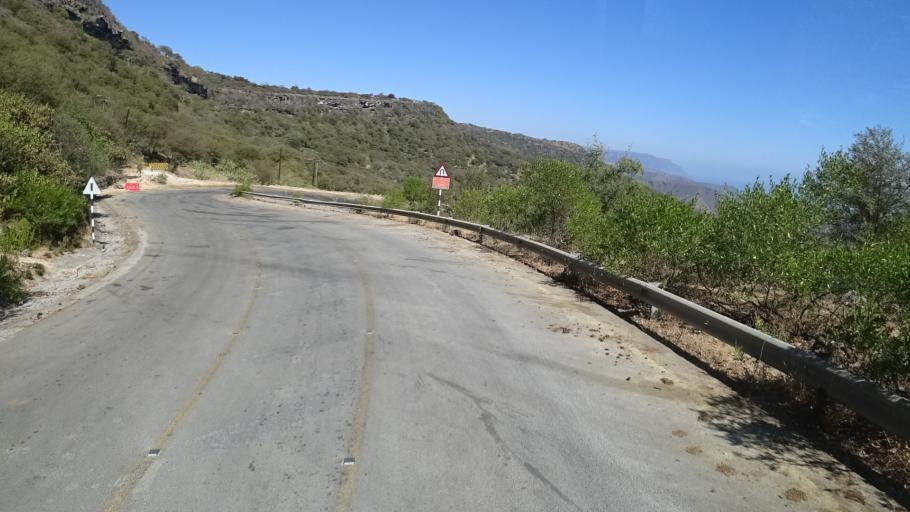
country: YE
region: Al Mahrah
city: Hawf
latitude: 16.7640
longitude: 53.3390
